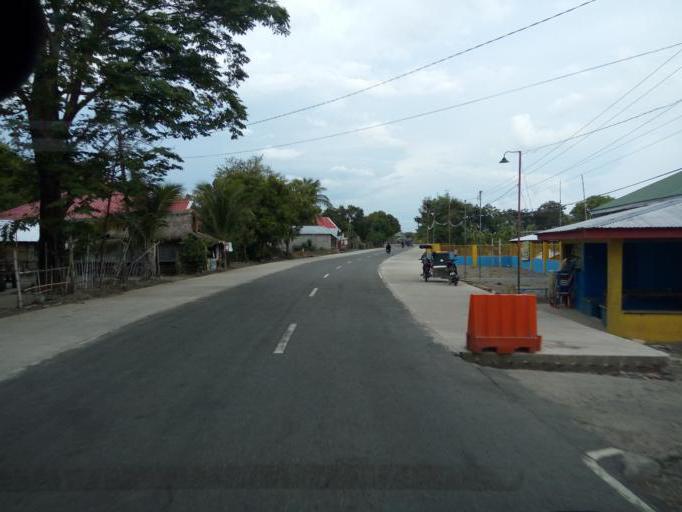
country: PH
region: Central Luzon
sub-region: Province of Nueva Ecija
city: Parista
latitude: 15.8392
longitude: 120.9367
